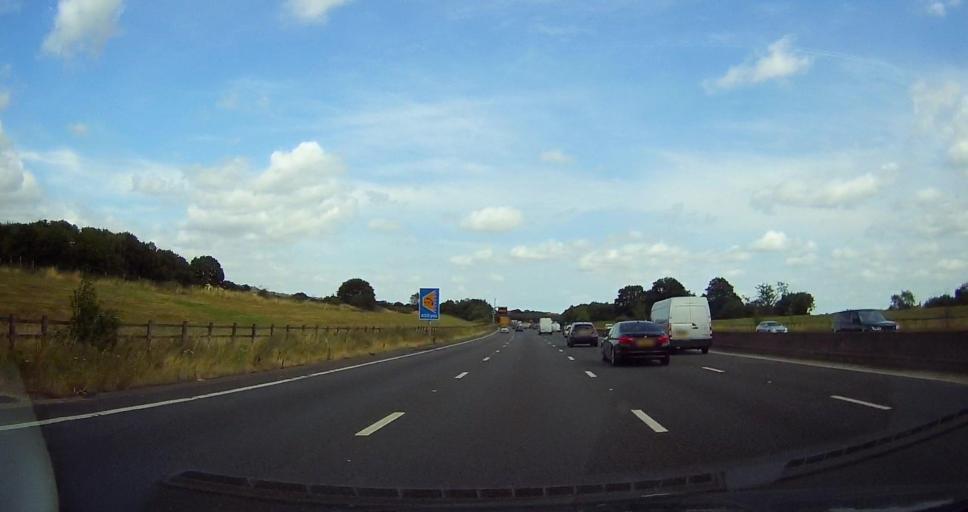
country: GB
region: England
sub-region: Kent
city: Westerham
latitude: 51.2751
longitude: 0.0691
